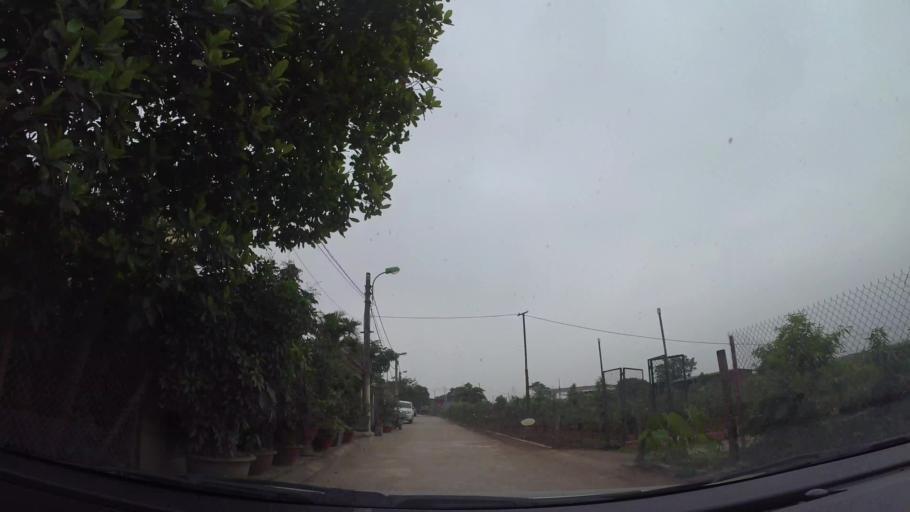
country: VN
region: Ha Noi
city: Tay Ho
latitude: 21.0746
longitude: 105.8279
